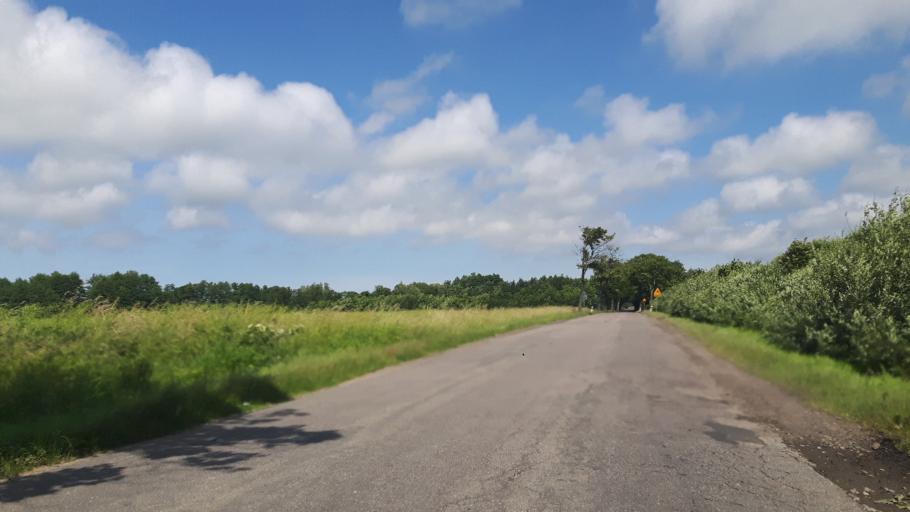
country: PL
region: Pomeranian Voivodeship
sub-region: Powiat slupski
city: Ustka
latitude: 54.5301
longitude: 16.8151
